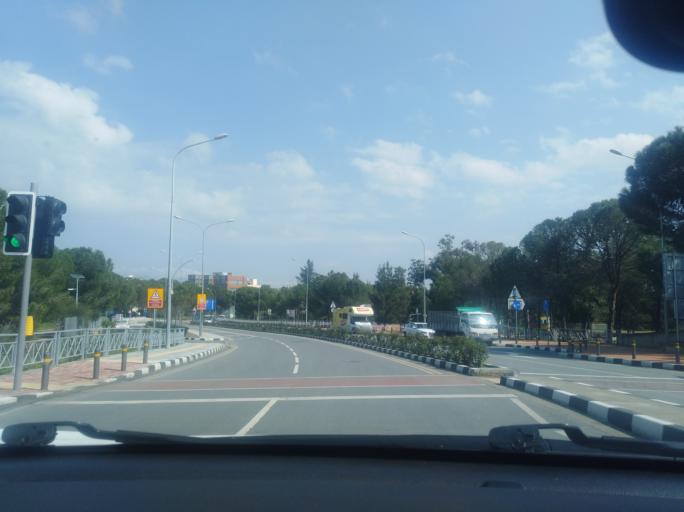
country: CY
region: Lefkosia
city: Nicosia
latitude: 35.1560
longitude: 33.3826
